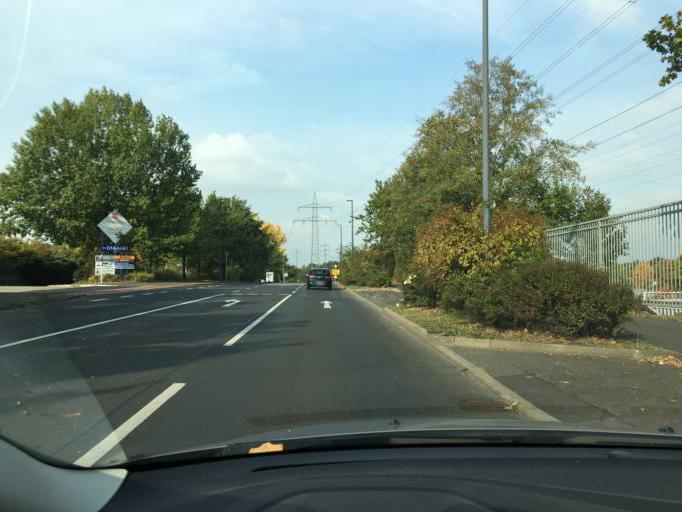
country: DE
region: Saxony
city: Kreischa
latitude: 50.9945
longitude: 13.7990
